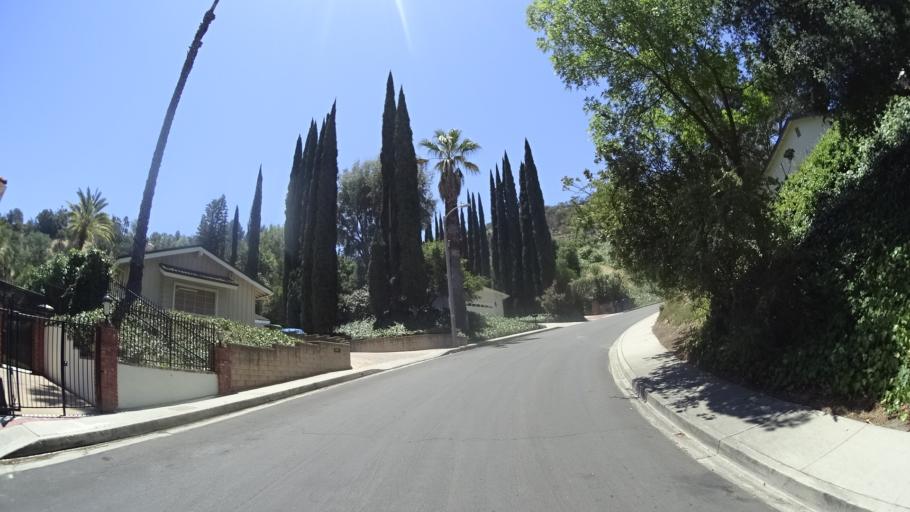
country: US
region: California
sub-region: Los Angeles County
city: Universal City
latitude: 34.1318
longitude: -118.3653
